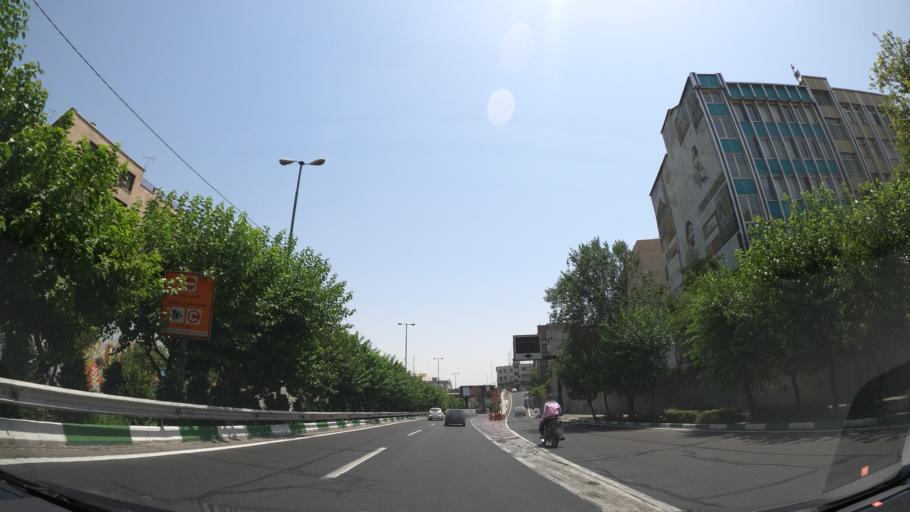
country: IR
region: Tehran
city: Tehran
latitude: 35.7255
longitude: 51.4244
